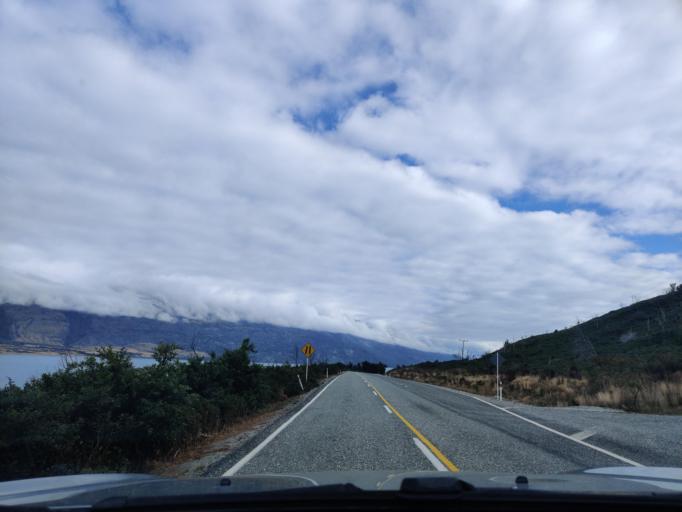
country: NZ
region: Otago
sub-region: Queenstown-Lakes District
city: Queenstown
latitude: -45.0793
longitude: 168.4688
